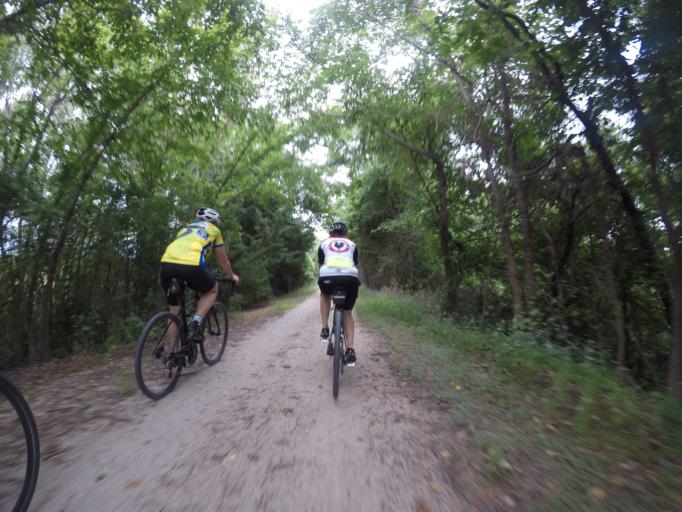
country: US
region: Kansas
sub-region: Anderson County
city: Garnett
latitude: 38.2582
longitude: -95.2505
